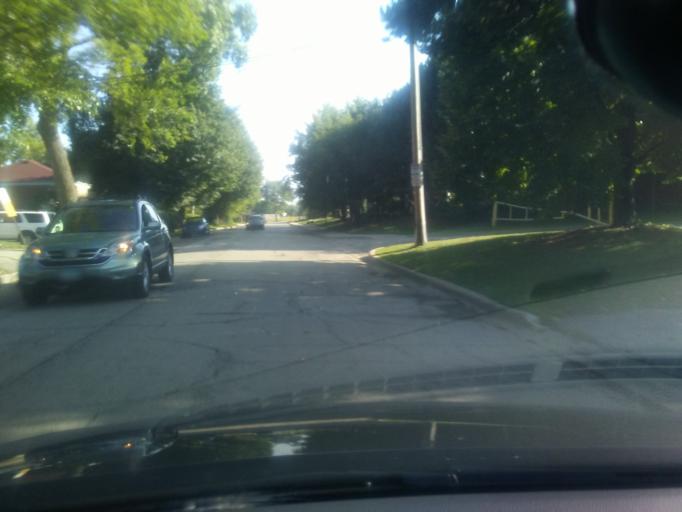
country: US
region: Illinois
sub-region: Cook County
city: Evanston
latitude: 42.0280
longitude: -87.7042
